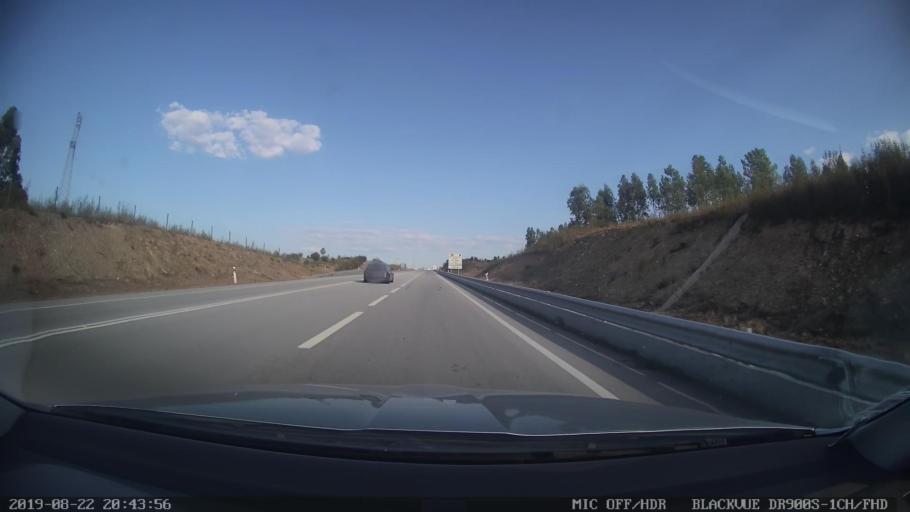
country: PT
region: Castelo Branco
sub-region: Proenca-A-Nova
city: Proenca-a-Nova
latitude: 39.7027
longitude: -7.8418
